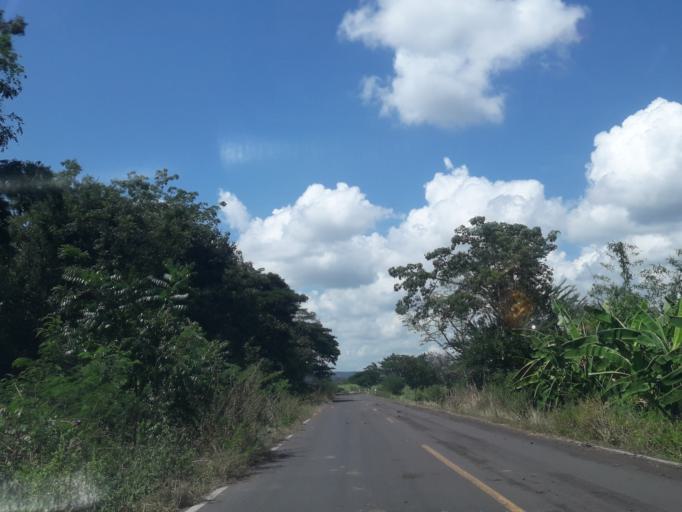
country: TH
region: Lop Buri
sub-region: Amphoe Tha Luang
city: Tha Luang
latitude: 15.0704
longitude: 101.0407
